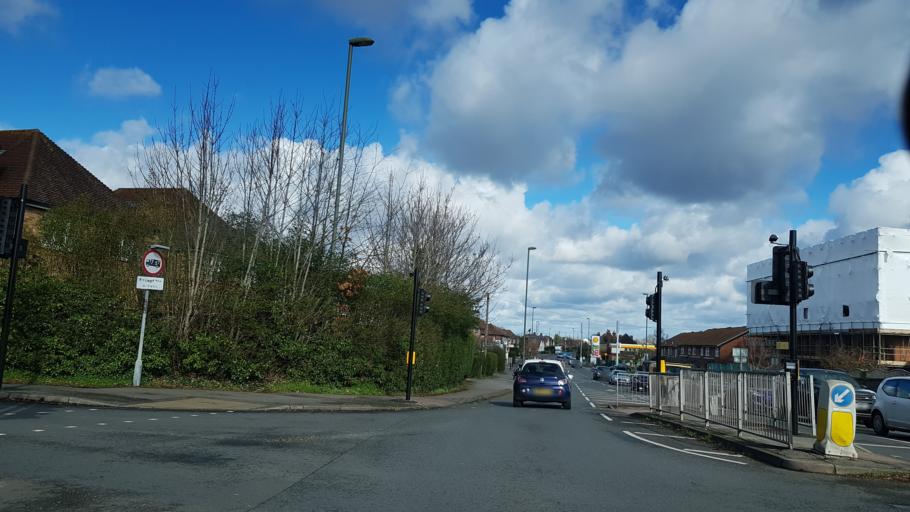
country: GB
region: England
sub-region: Surrey
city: Guildford
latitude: 51.2550
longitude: -0.5936
